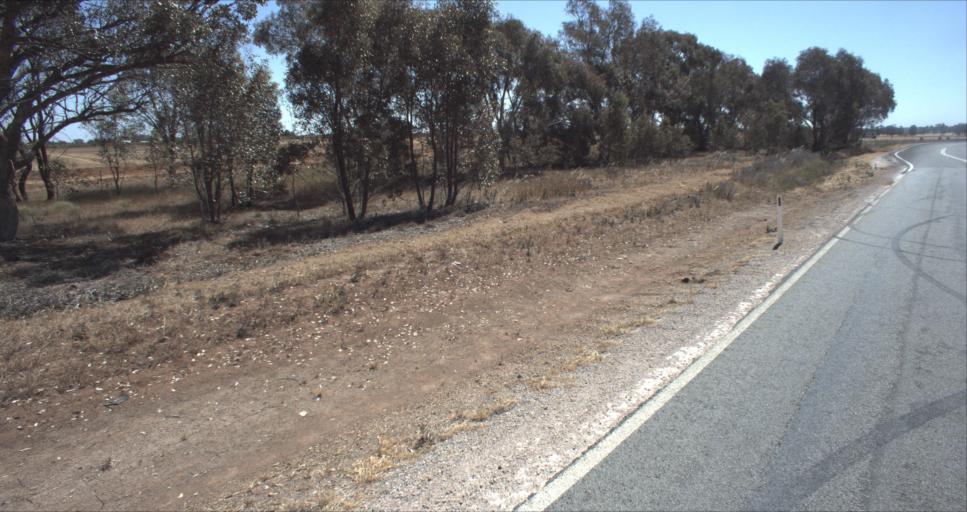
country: AU
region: New South Wales
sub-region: Leeton
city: Leeton
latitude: -34.4948
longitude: 146.4326
